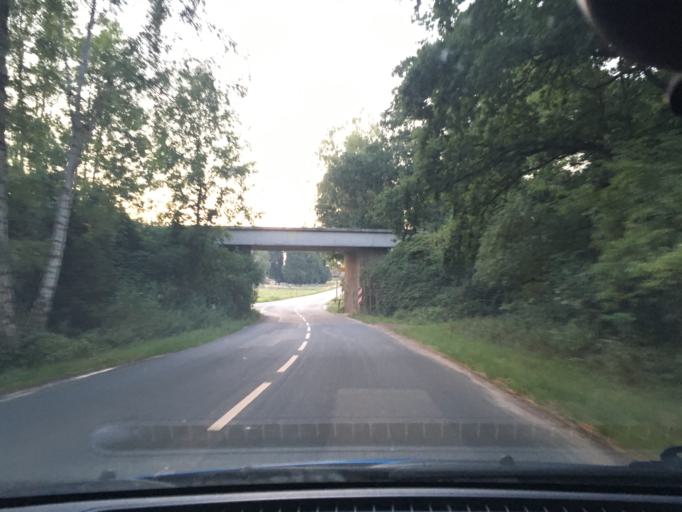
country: DE
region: Lower Saxony
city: Embsen
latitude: 53.1568
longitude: 10.3470
